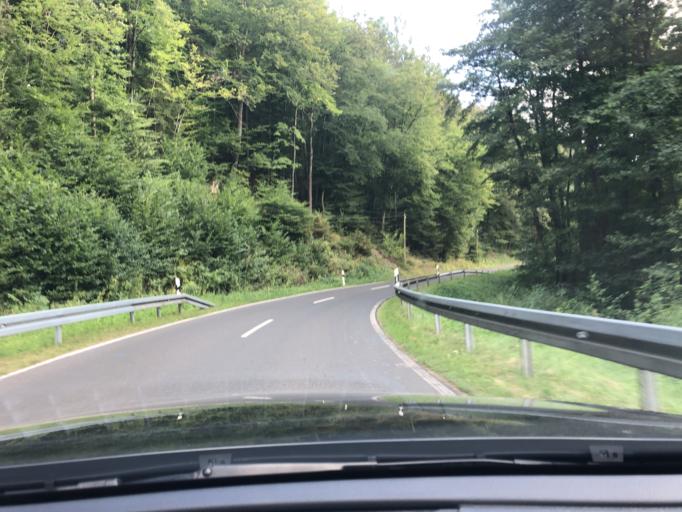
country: DE
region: Bavaria
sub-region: Regierungsbezirk Unterfranken
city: Breitbrunn
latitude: 50.0282
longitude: 10.6795
